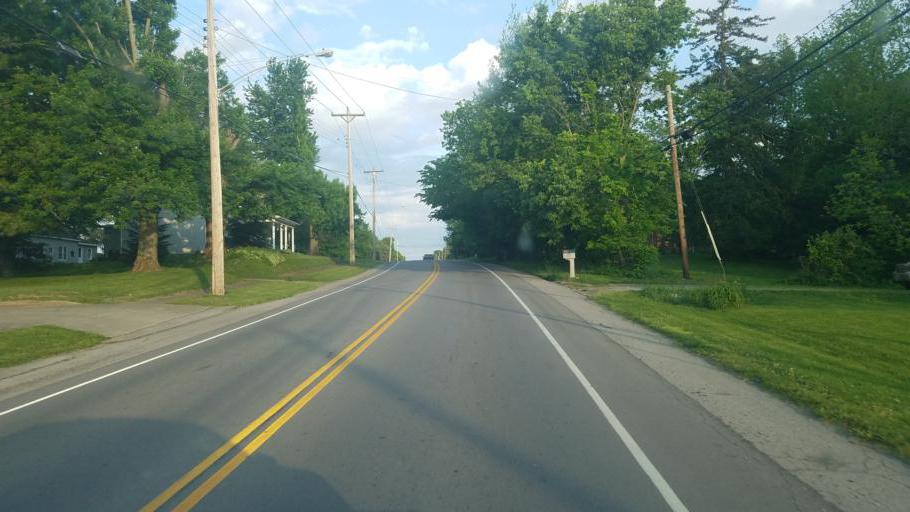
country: US
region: Ohio
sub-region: Highland County
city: Leesburg
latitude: 39.3460
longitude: -83.5621
